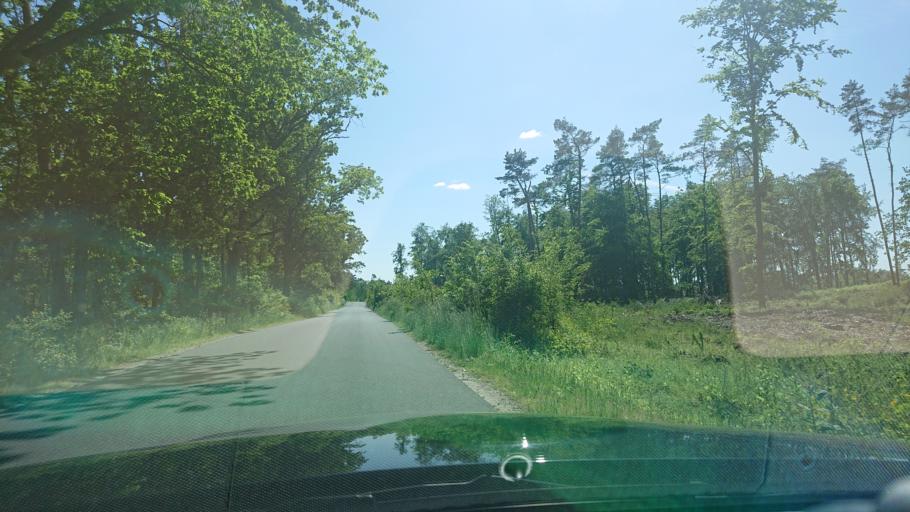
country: PL
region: Greater Poland Voivodeship
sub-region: Powiat gnieznienski
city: Gniezno
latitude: 52.4953
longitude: 17.5803
